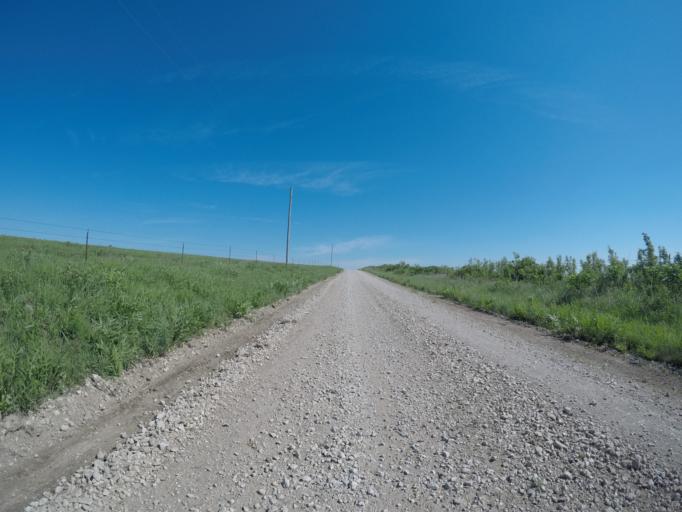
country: US
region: Kansas
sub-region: Wabaunsee County
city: Alma
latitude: 38.9546
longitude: -96.1137
